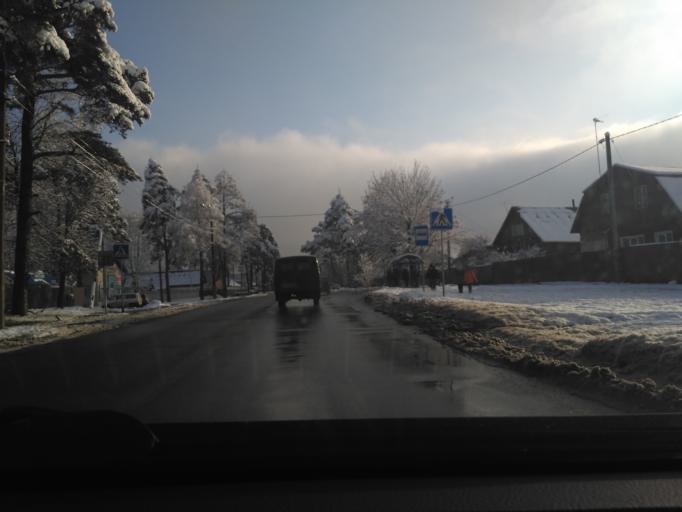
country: BY
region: Minsk
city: Horad Barysaw
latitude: 54.2328
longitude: 28.4891
